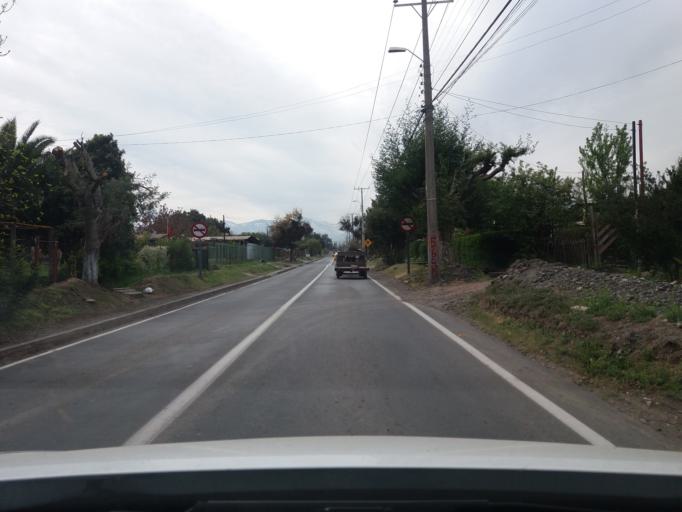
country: CL
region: Valparaiso
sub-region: Provincia de Los Andes
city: Los Andes
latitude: -32.8242
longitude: -70.6629
